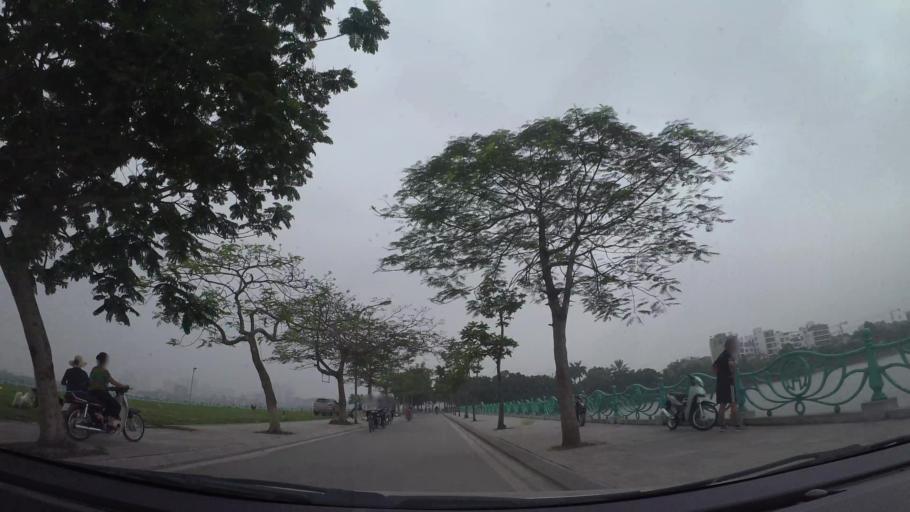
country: VN
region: Ha Noi
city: Tay Ho
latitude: 21.0582
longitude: 105.8193
